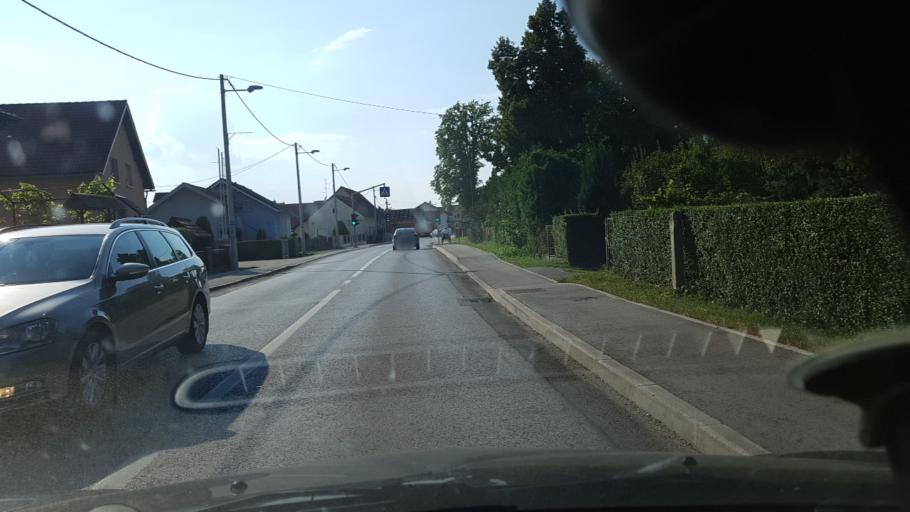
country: HR
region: Zagrebacka
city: Brdovec
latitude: 45.8650
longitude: 15.7686
